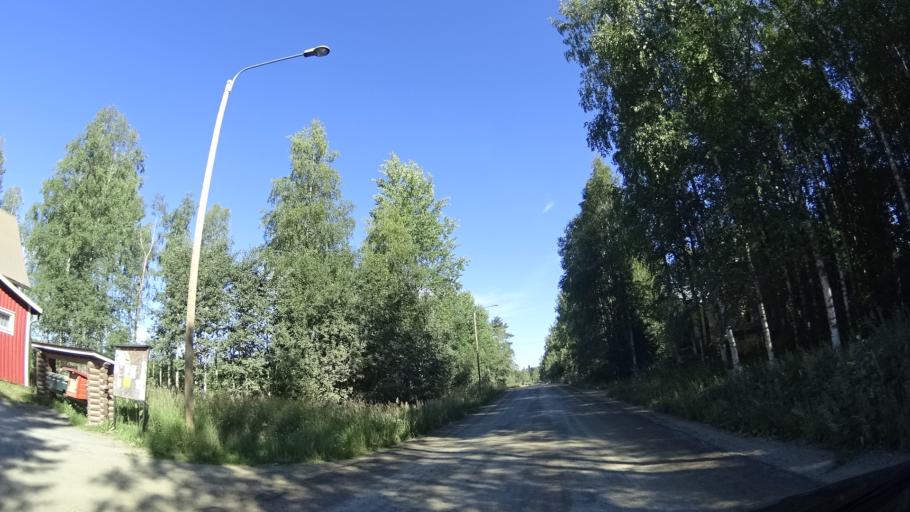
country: FI
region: Central Finland
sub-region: Jyvaeskylae
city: Petaejaevesi
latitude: 62.3559
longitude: 25.3232
